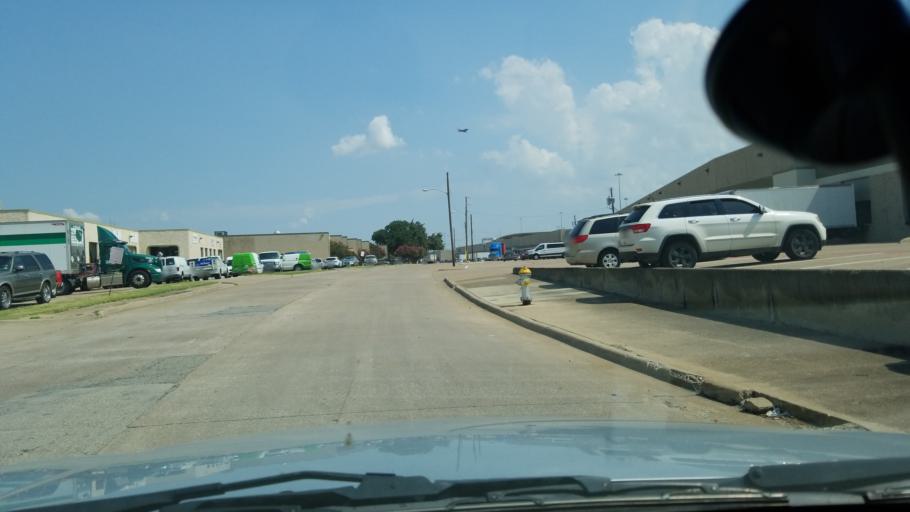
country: US
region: Texas
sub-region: Dallas County
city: Farmers Branch
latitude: 32.8667
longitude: -96.9006
